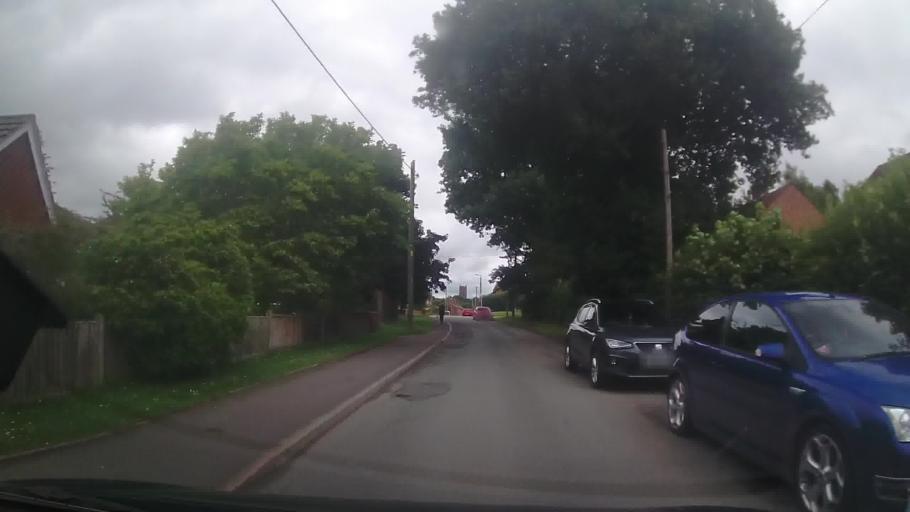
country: GB
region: England
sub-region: Shropshire
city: Whitchurch
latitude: 52.9691
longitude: -2.6949
